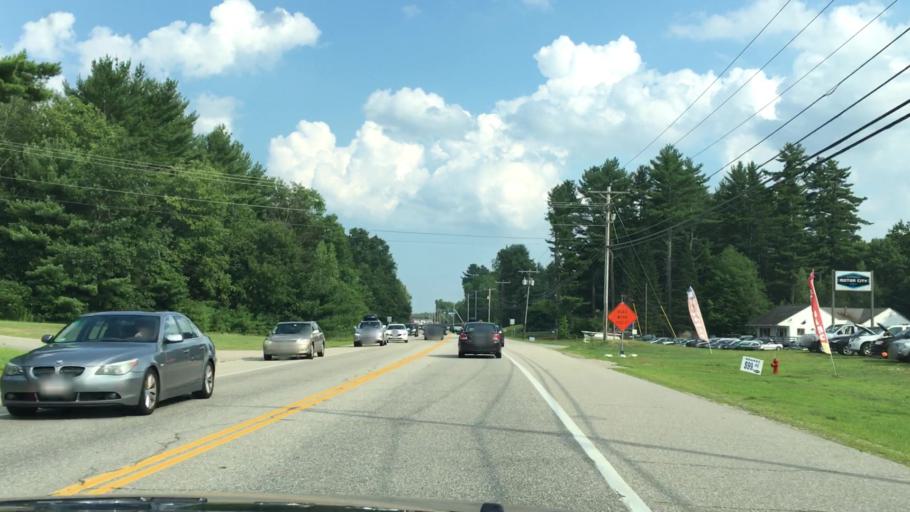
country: US
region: New Hampshire
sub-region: Strafford County
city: Rochester
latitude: 43.3404
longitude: -71.0174
